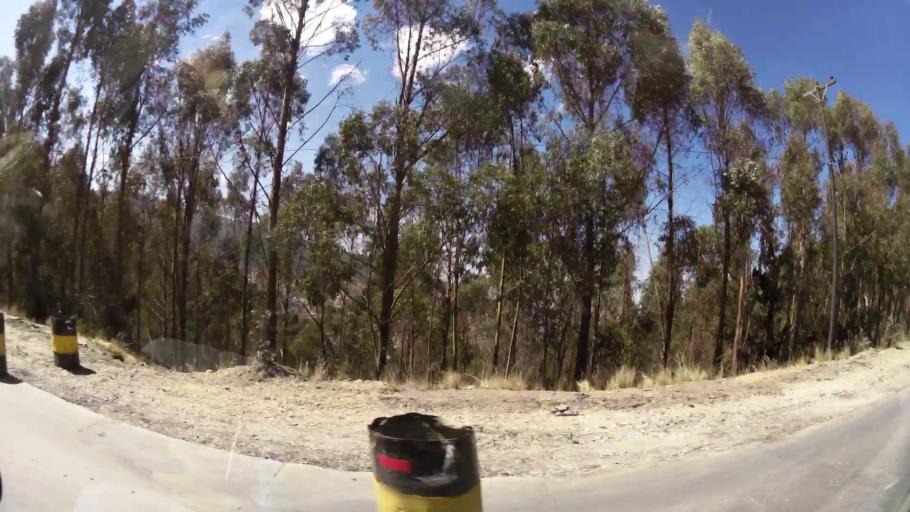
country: BO
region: La Paz
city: La Paz
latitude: -16.4769
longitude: -68.1596
